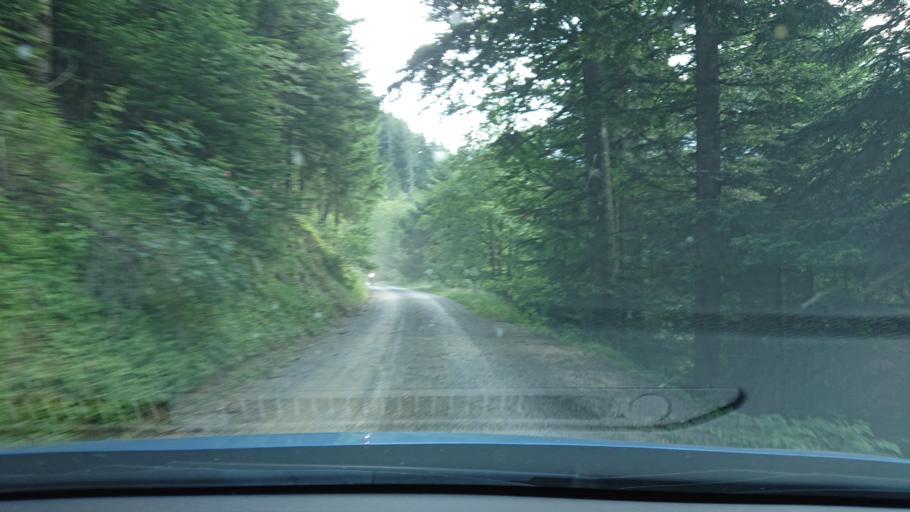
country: FR
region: Rhone-Alpes
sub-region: Departement de l'Isere
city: Mens
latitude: 44.7900
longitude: 5.8834
